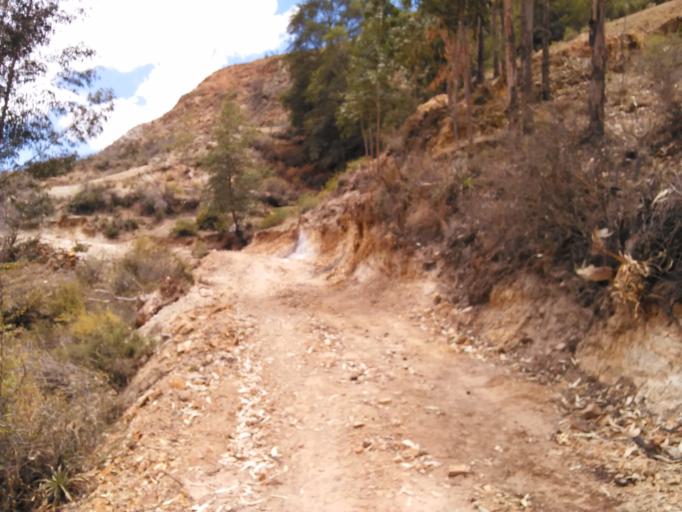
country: PE
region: Ayacucho
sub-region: Provincia de Victor Fajardo
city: Canaria
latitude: -13.8843
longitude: -73.9428
